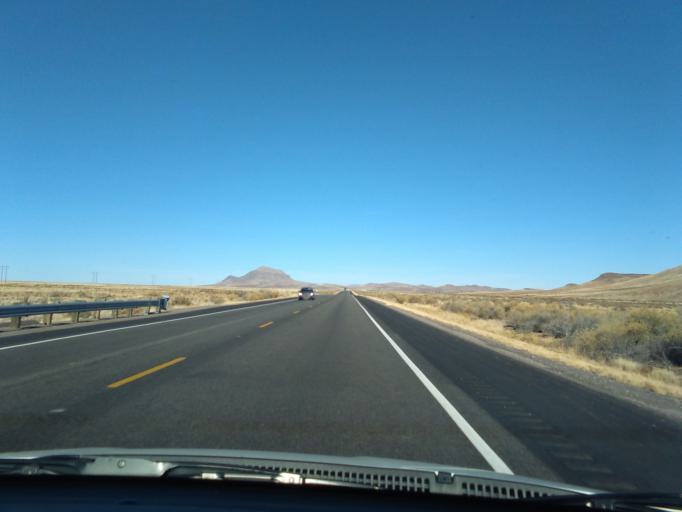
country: US
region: New Mexico
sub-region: Dona Ana County
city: Hatch
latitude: 32.5345
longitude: -107.4871
